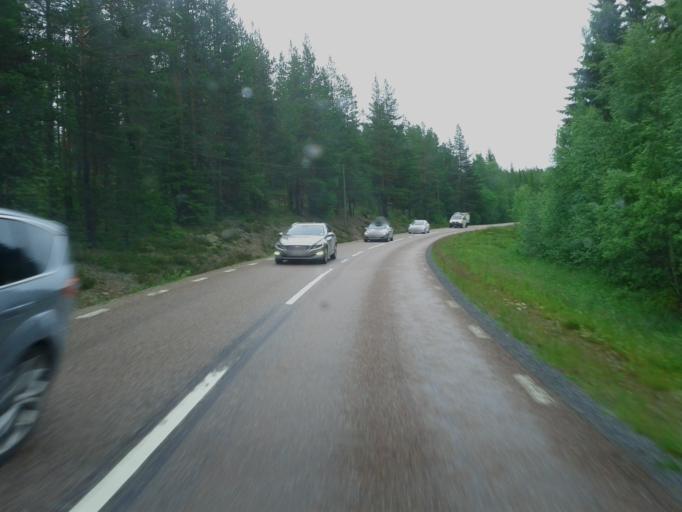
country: NO
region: Hedmark
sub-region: Trysil
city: Innbygda
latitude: 61.8295
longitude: 12.8620
